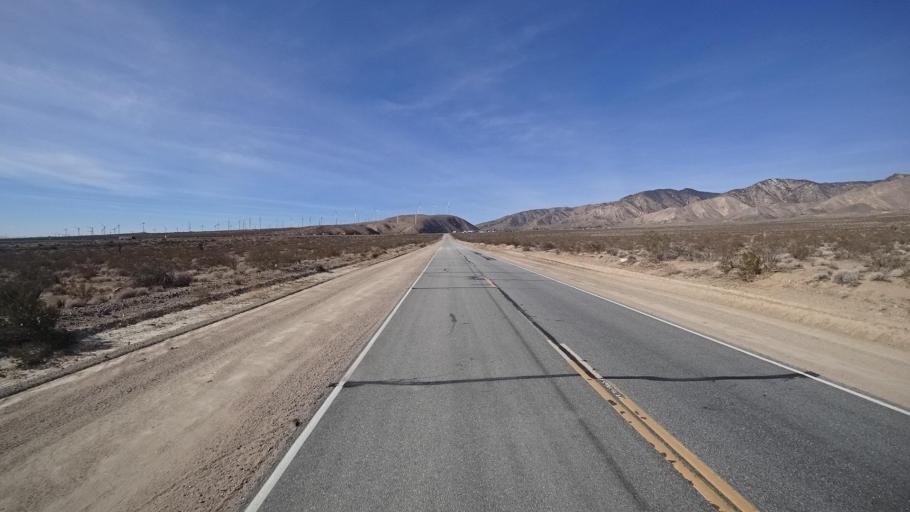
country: US
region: California
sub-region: Kern County
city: Mojave
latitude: 35.1232
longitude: -118.1933
